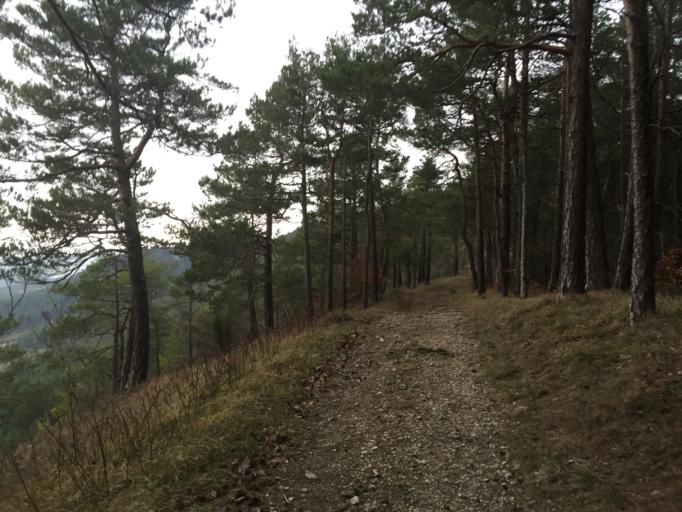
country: DE
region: Thuringia
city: Bad Blankenburg
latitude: 50.7074
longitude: 11.2342
